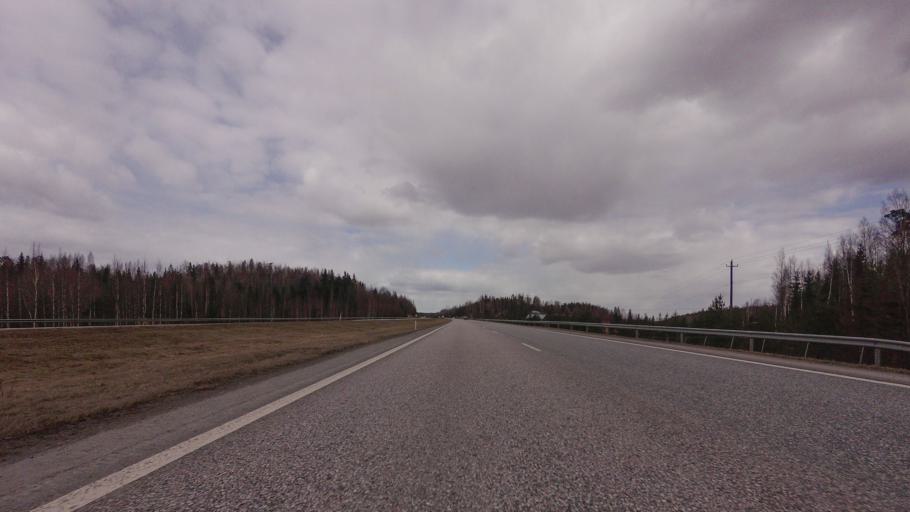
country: FI
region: Uusimaa
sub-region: Helsinki
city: Nurmijaervi
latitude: 60.3802
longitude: 24.8150
